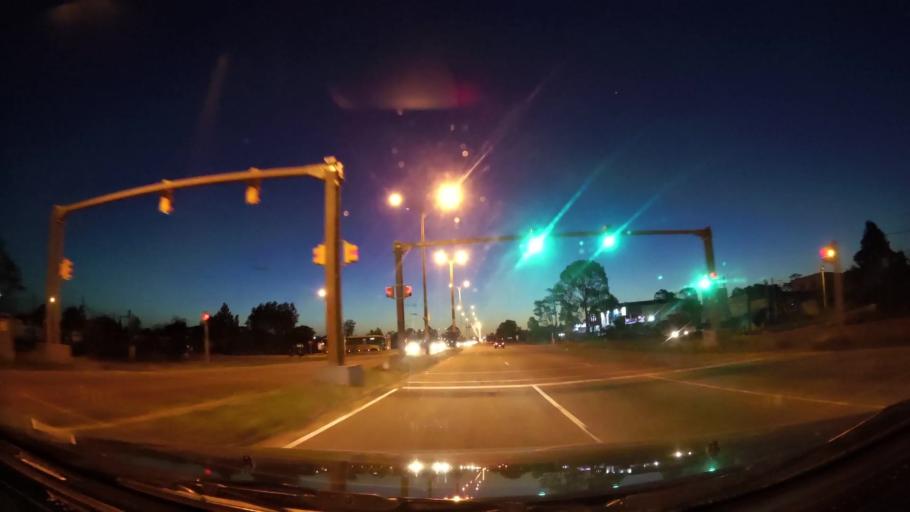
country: UY
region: Canelones
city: Colonia Nicolich
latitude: -34.8158
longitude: -55.9472
